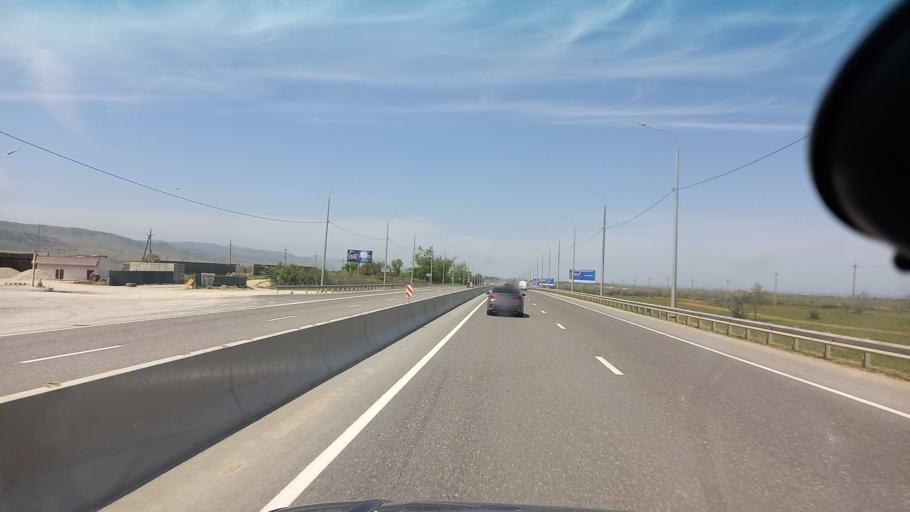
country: RU
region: Dagestan
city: Manas
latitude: 42.7321
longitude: 47.6639
